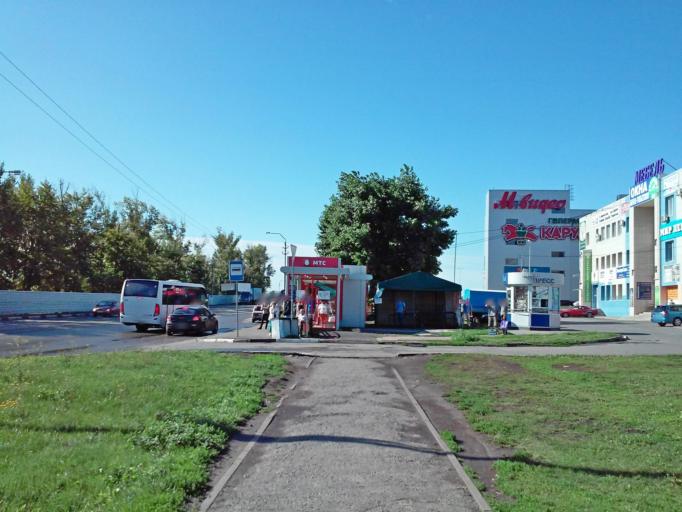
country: RU
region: Belgorod
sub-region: Belgorodskiy Rayon
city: Belgorod
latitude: 50.5539
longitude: 36.5725
